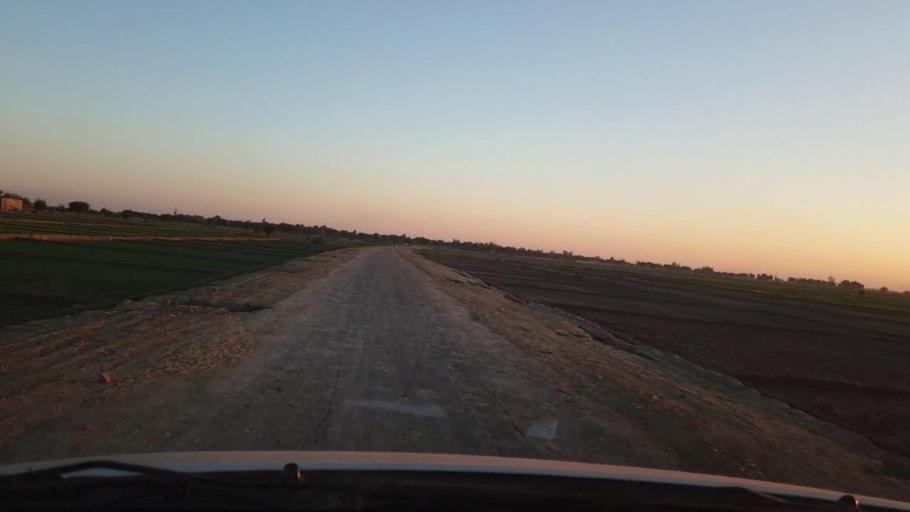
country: PK
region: Sindh
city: Johi
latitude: 26.8379
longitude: 67.4414
